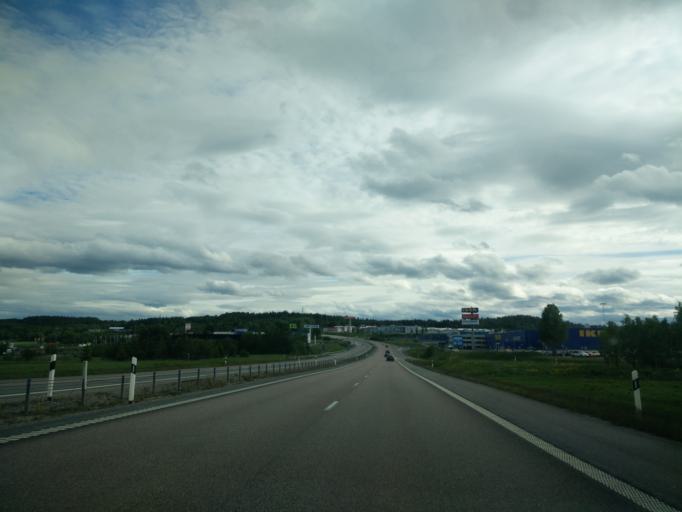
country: SE
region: Vaesternorrland
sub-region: Sundsvalls Kommun
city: Sundsbruk
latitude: 62.4482
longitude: 17.3411
